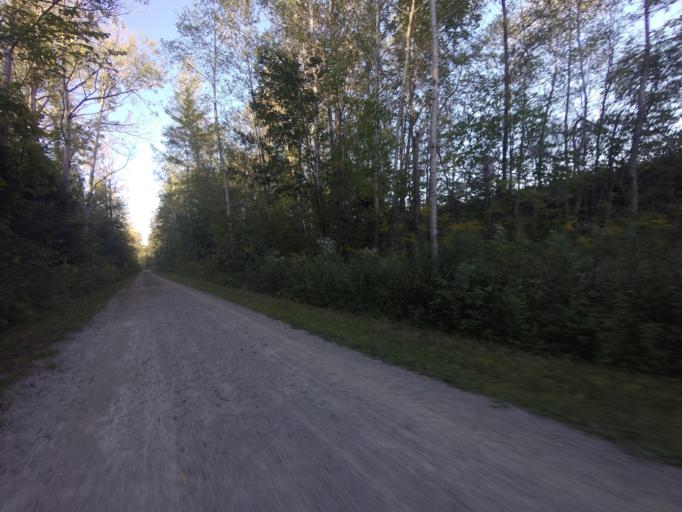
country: CA
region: Ontario
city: Brampton
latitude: 43.8493
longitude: -79.8799
